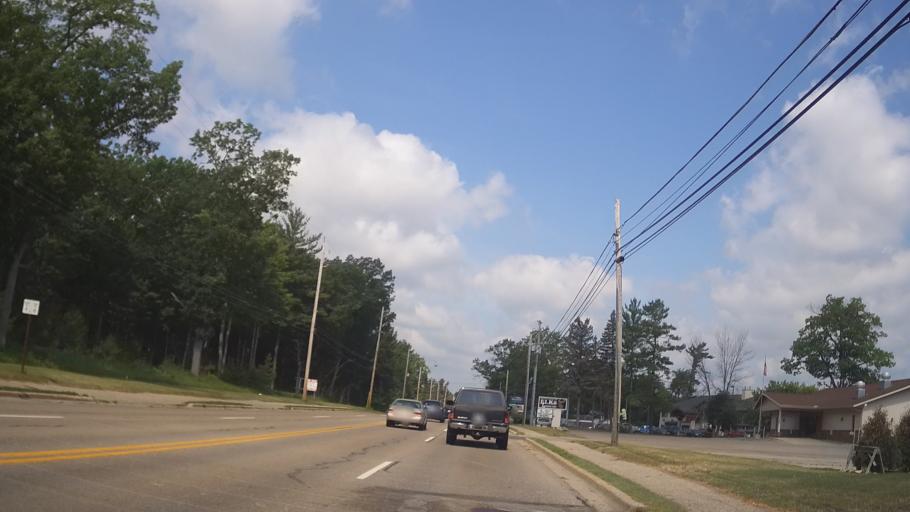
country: US
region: Michigan
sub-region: Roscommon County
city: Houghton Lake
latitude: 44.2990
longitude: -84.7369
